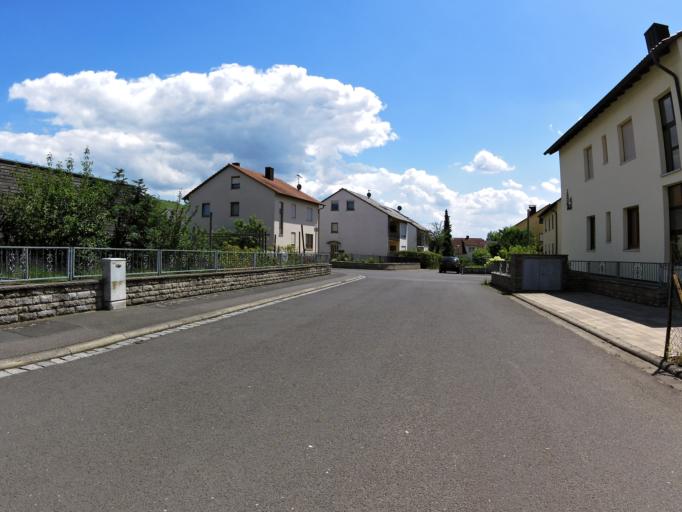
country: DE
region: Bavaria
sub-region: Regierungsbezirk Unterfranken
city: Thungersheim
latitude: 49.8777
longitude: 9.8464
